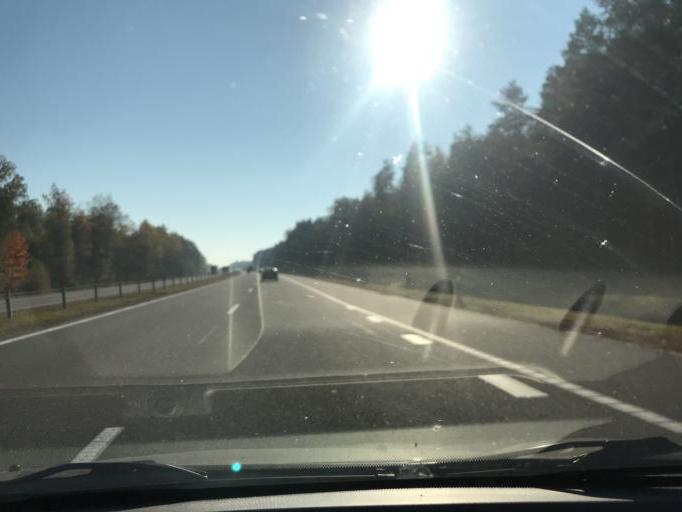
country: BY
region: Minsk
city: Pukhavichy
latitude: 53.5152
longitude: 28.2932
